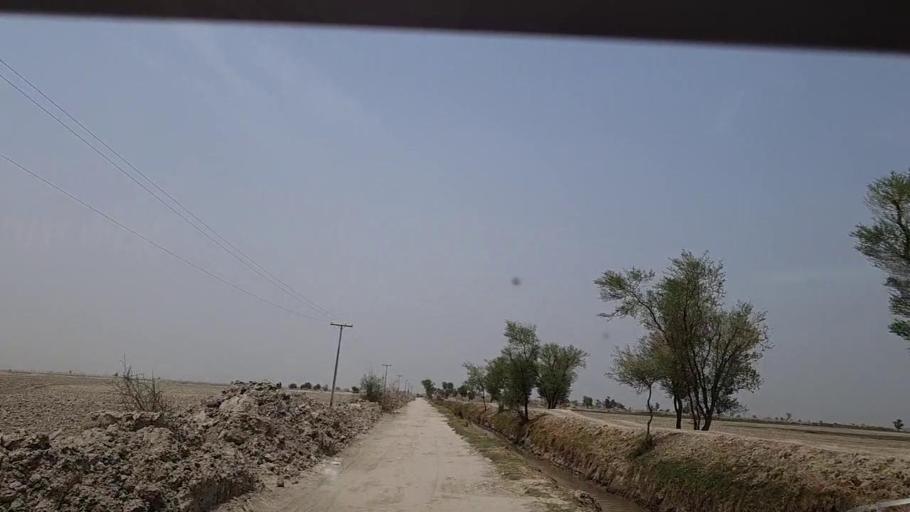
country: PK
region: Sindh
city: Khairpur Nathan Shah
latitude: 27.0489
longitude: 67.6191
